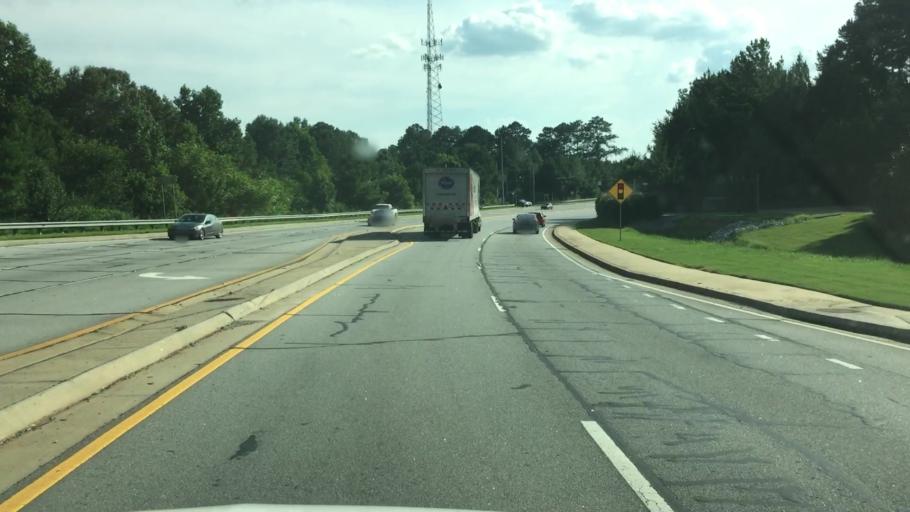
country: US
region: Georgia
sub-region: Rockdale County
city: Lakeview Estates
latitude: 33.7742
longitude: -84.0488
